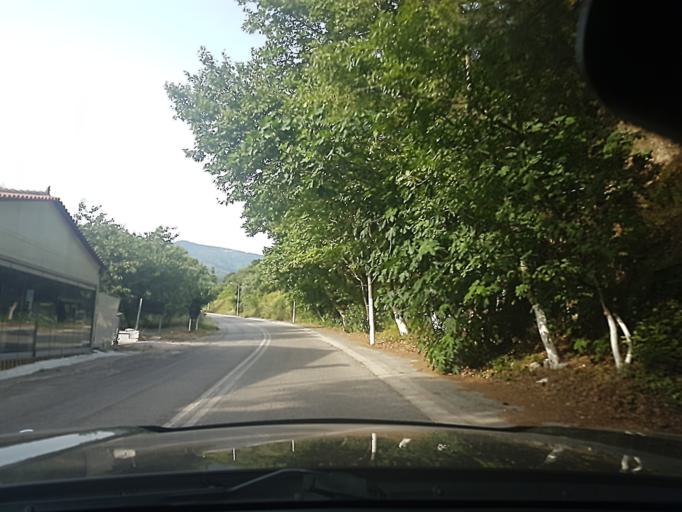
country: GR
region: Central Greece
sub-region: Nomos Evvoias
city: Yimnon
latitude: 38.5756
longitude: 23.8314
